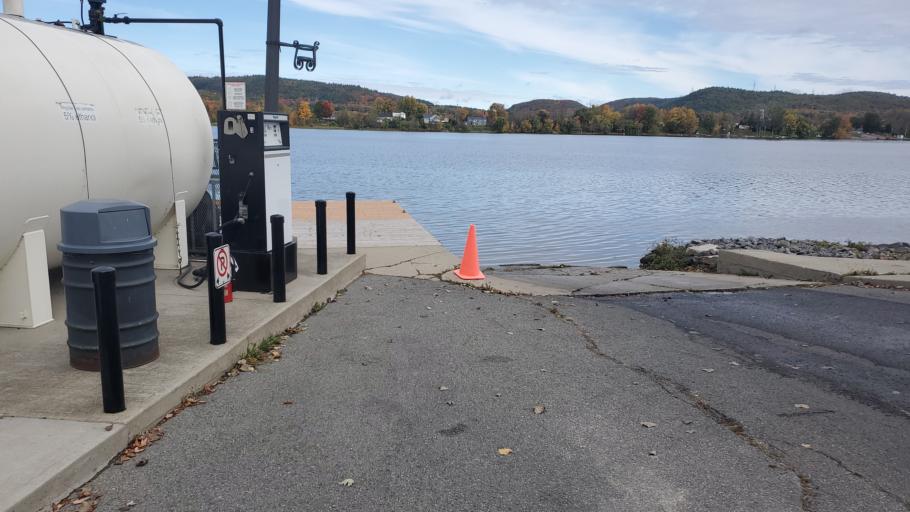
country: CA
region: Quebec
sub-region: Outaouais
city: Papineauville
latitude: 45.6404
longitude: -74.8899
